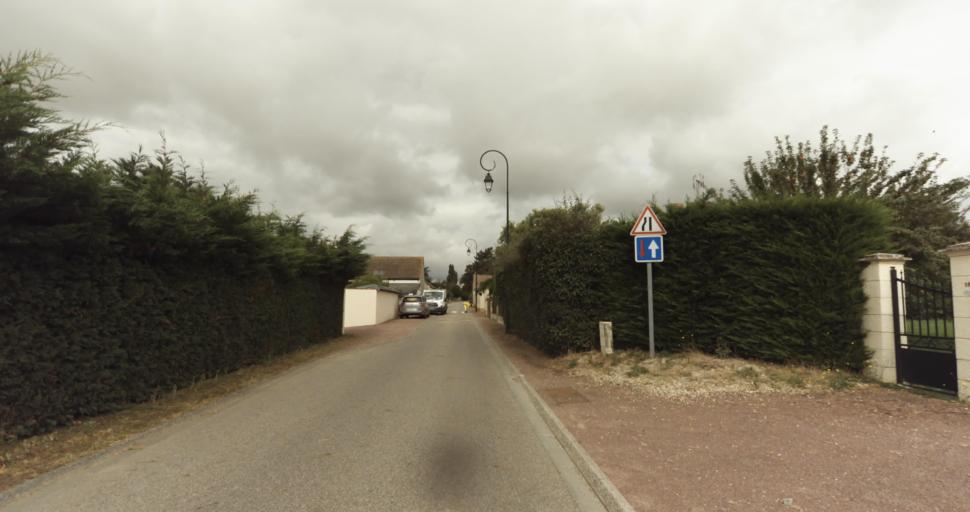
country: FR
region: Haute-Normandie
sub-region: Departement de l'Eure
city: Menilles
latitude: 48.9586
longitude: 1.2947
